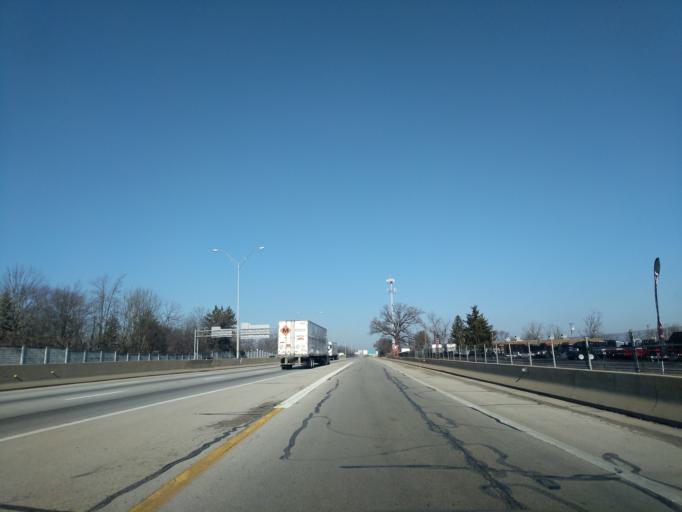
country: US
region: Ohio
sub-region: Montgomery County
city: Northridge
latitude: 39.8215
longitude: -84.1890
